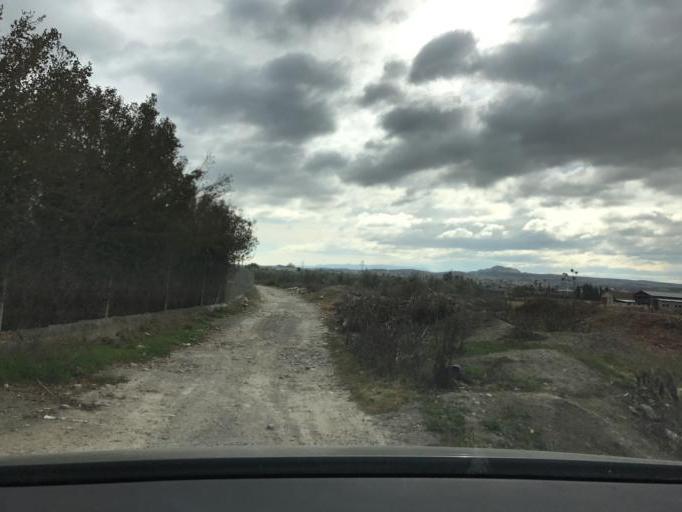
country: ES
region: Andalusia
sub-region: Provincia de Granada
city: Cullar-Vega
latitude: 37.1607
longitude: -3.6606
